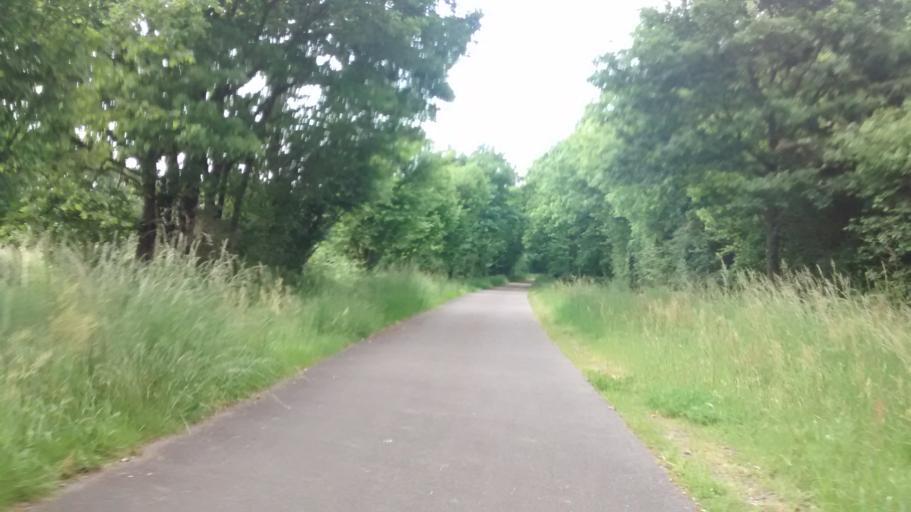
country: FR
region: Brittany
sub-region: Departement du Morbihan
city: Molac
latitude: 47.7133
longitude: -2.4224
